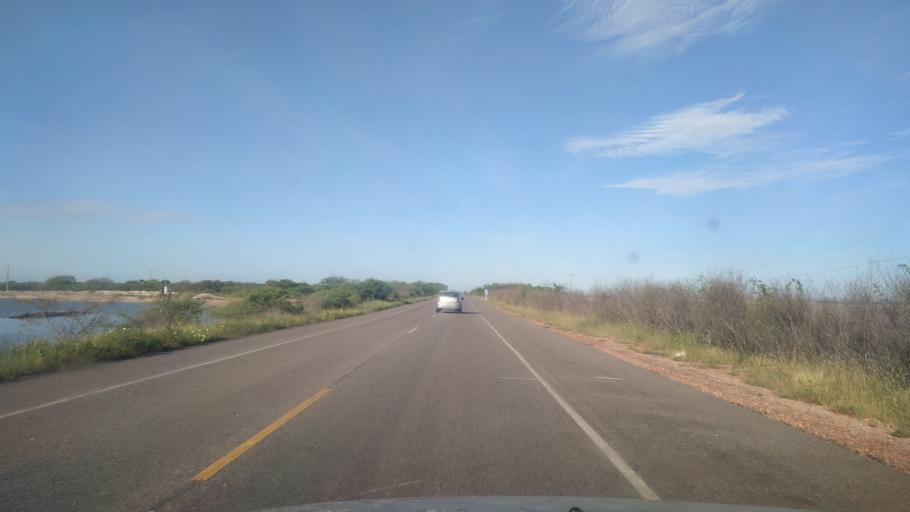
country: BR
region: Rio Grande do Norte
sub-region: Areia Branca
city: Areia Branca
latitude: -5.0436
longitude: -37.1410
